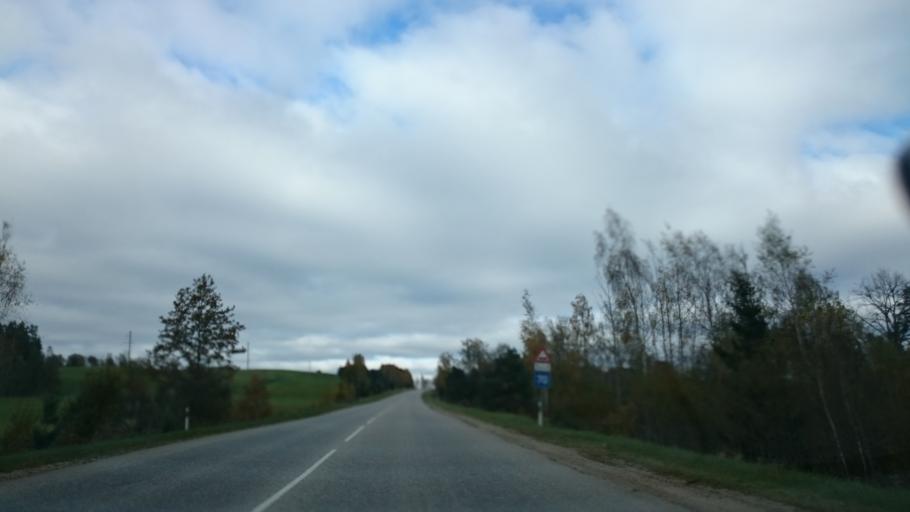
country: LV
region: Amatas Novads
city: Drabesi
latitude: 57.2616
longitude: 25.2683
